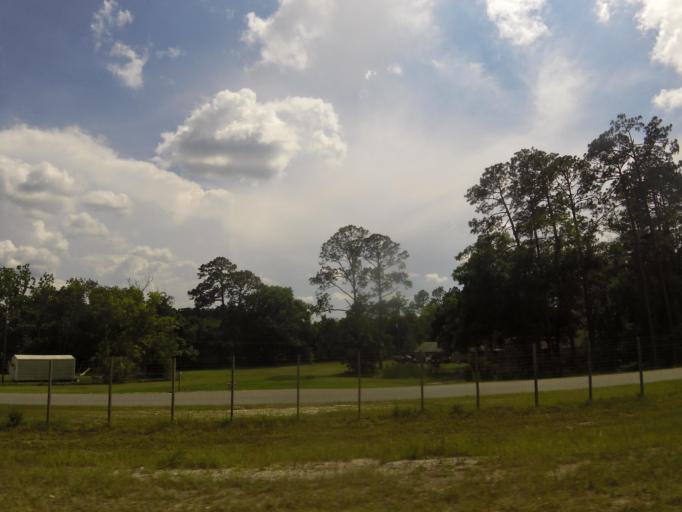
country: US
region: Florida
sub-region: Duval County
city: Baldwin
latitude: 30.2957
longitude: -81.9875
